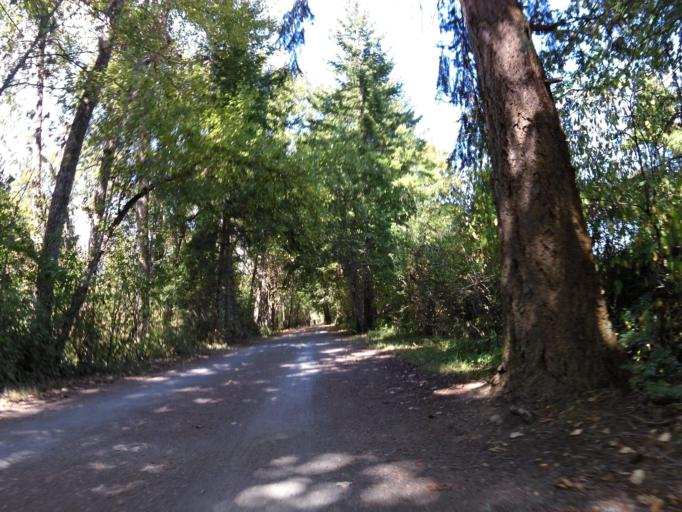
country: CA
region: British Columbia
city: Victoria
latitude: 48.5375
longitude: -123.3793
